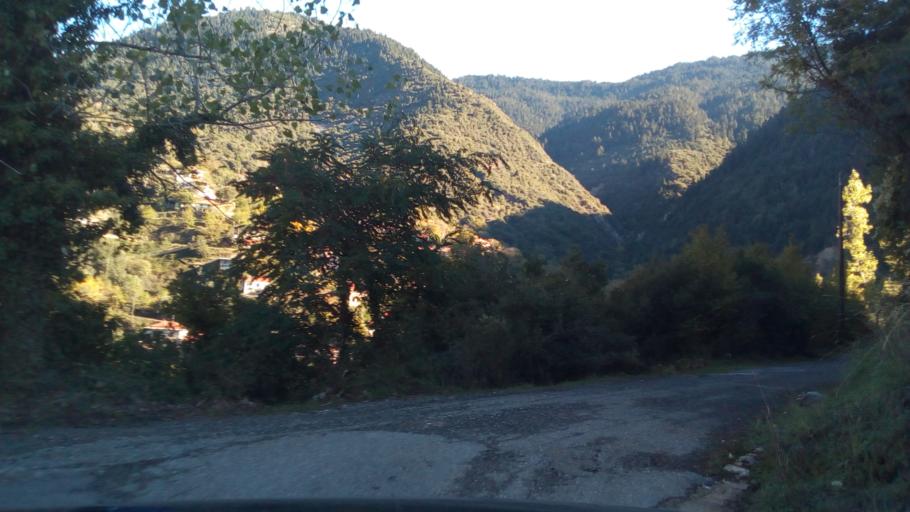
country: GR
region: West Greece
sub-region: Nomos Aitolias kai Akarnanias
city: Nafpaktos
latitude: 38.5622
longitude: 21.8522
